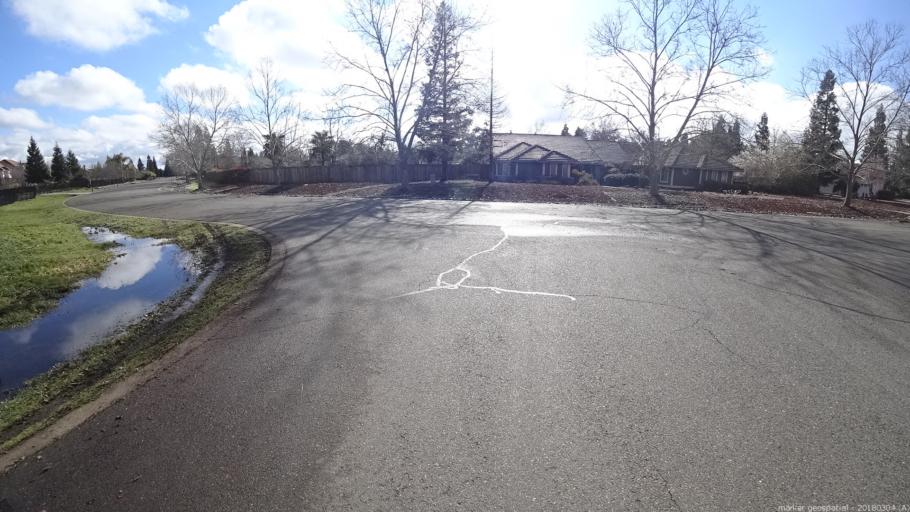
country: US
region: California
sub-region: Sacramento County
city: Vineyard
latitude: 38.4606
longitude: -121.3143
